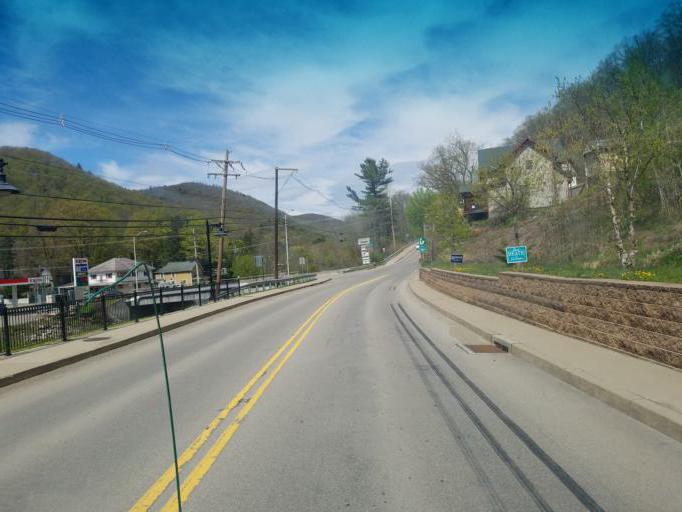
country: US
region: Pennsylvania
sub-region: Potter County
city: Galeton
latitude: 41.7356
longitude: -77.6468
